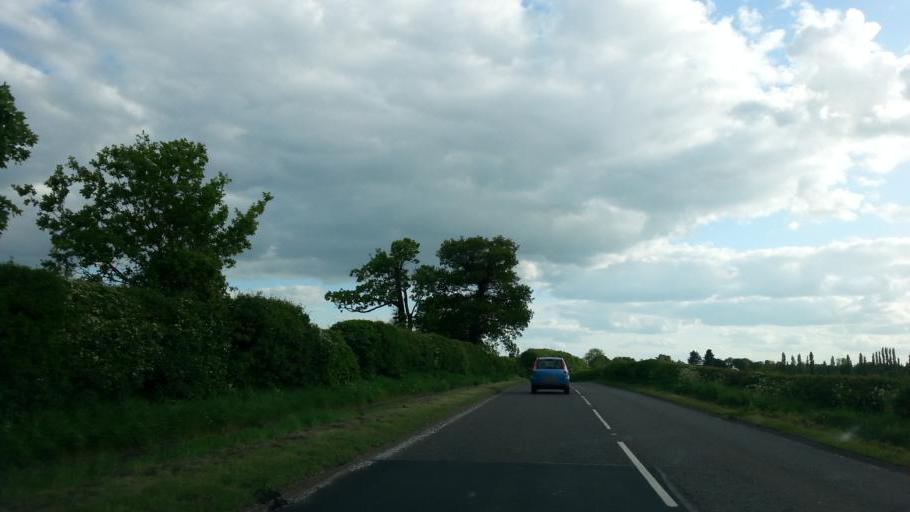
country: GB
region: England
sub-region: Nottinghamshire
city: South Collingham
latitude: 53.1101
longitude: -0.7762
